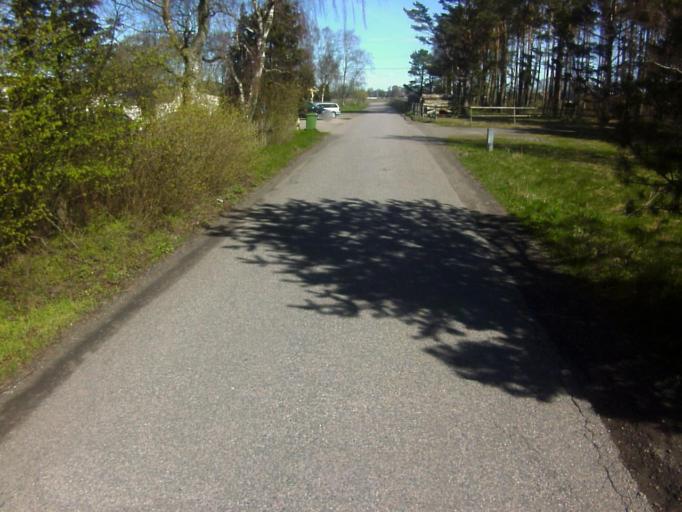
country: SE
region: Skane
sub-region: Kavlinge Kommun
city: Hofterup
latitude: 55.8163
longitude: 12.9957
